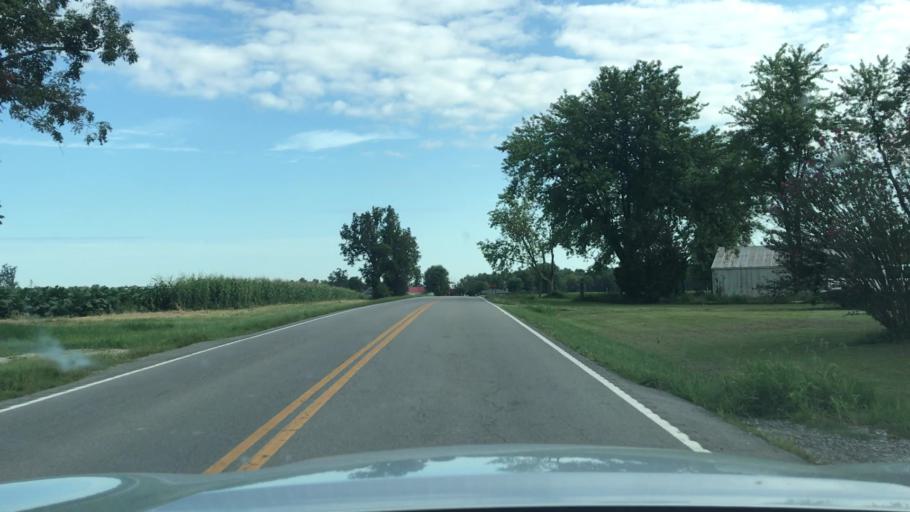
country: US
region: Kentucky
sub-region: Todd County
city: Elkton
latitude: 36.8558
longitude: -87.1587
